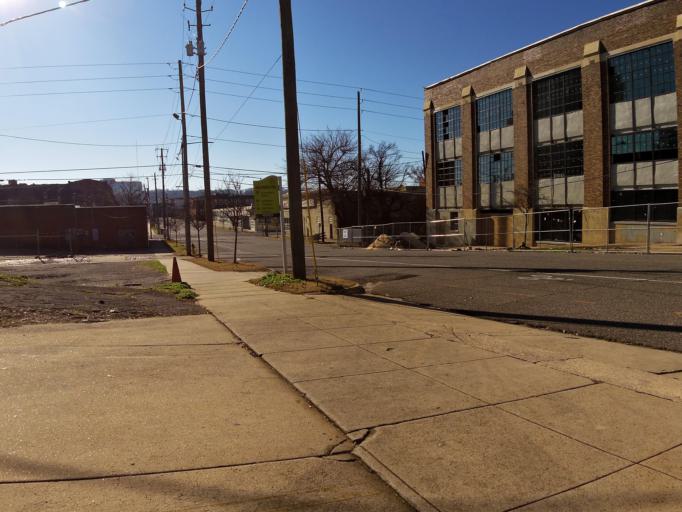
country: US
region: Alabama
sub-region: Jefferson County
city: Birmingham
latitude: 33.5135
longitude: -86.8123
